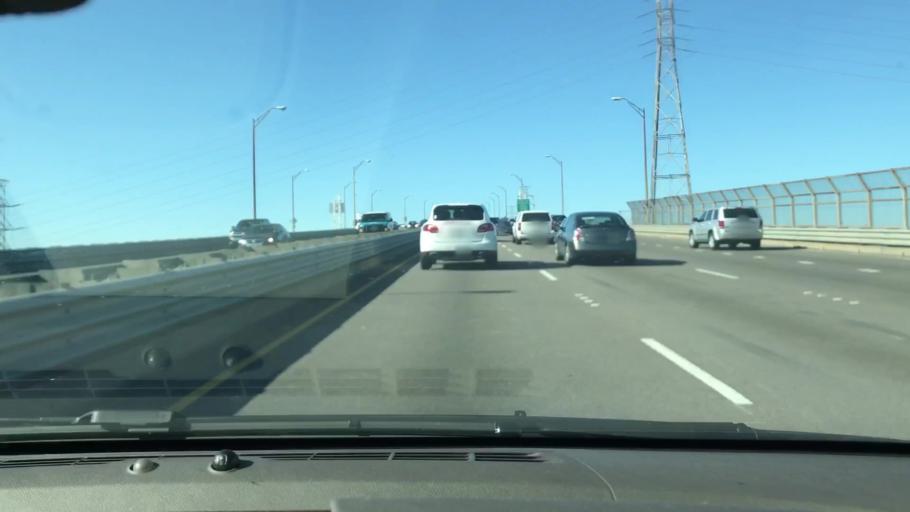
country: US
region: Louisiana
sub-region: Saint Bernard Parish
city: Arabi
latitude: 30.0060
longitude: -90.0209
